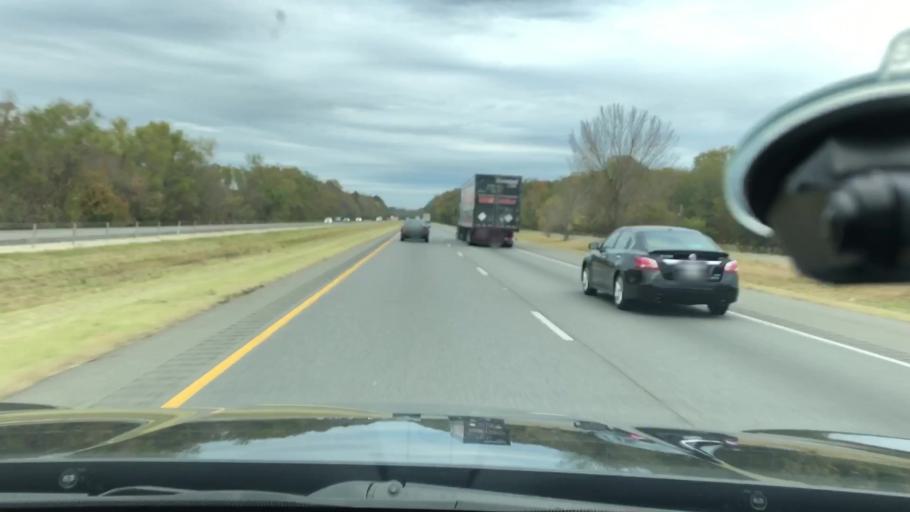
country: US
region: Arkansas
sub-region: Hot Spring County
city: Malvern
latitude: 34.3629
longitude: -92.8720
